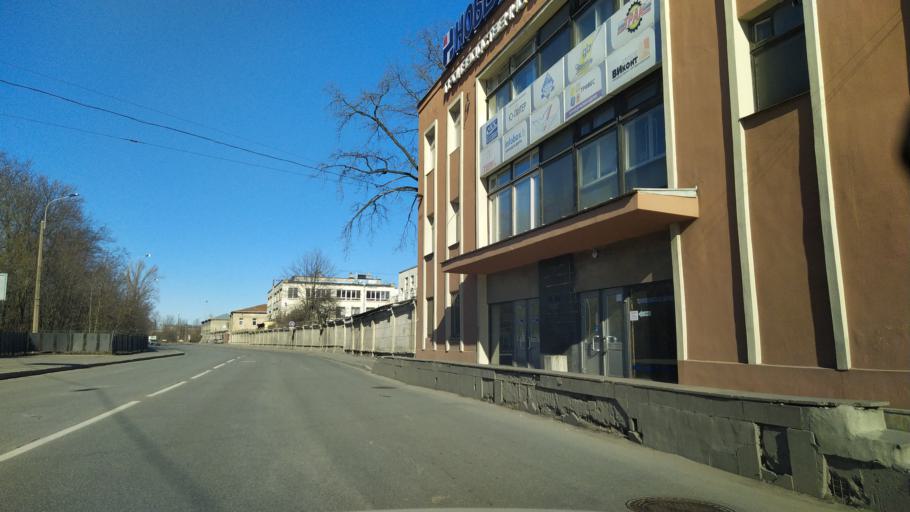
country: RU
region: St.-Petersburg
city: Centralniy
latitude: 59.9006
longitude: 30.3729
